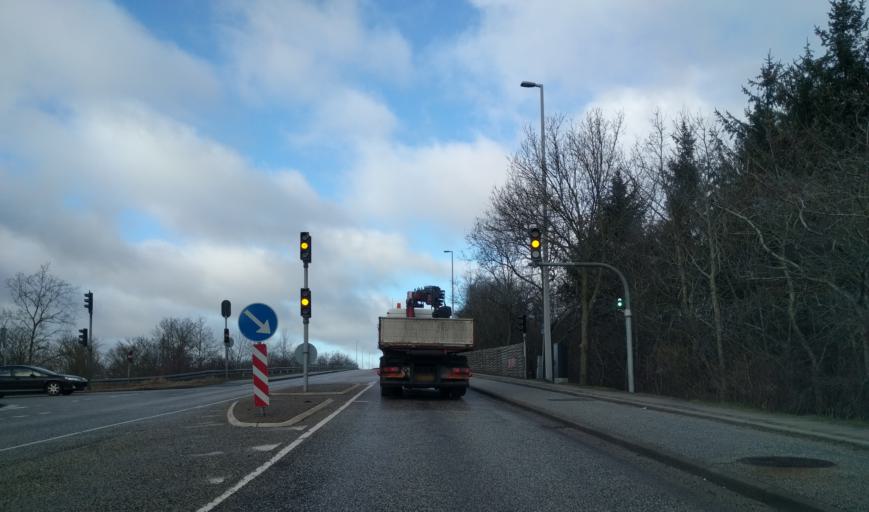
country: DK
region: North Denmark
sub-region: Alborg Kommune
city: Aalborg
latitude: 57.0132
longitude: 9.9019
